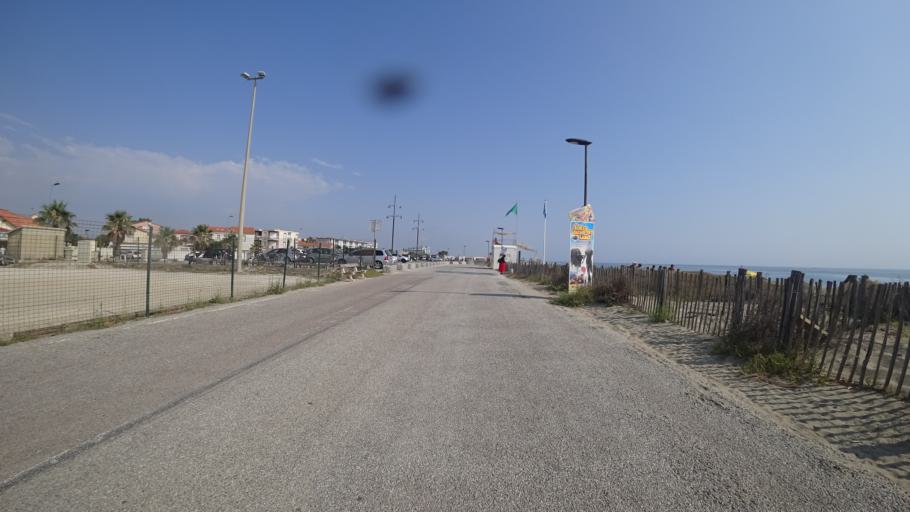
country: FR
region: Languedoc-Roussillon
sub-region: Departement des Pyrenees-Orientales
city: Saint-Cyprien-Plage
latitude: 42.6331
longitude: 3.0354
